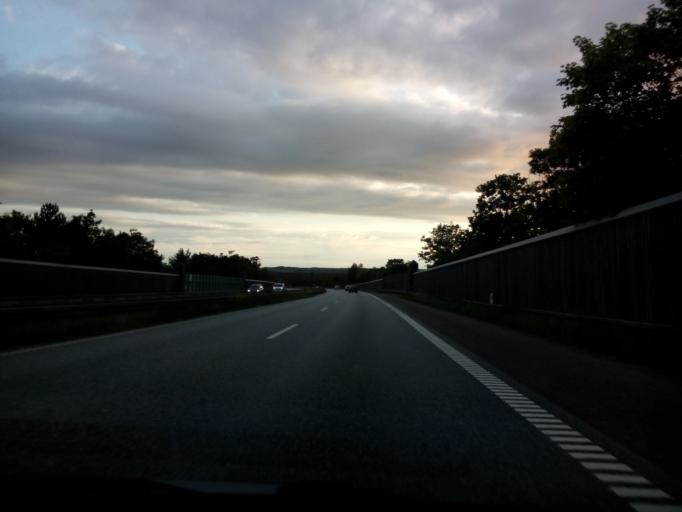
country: DK
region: North Denmark
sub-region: Alborg Kommune
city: Aalborg
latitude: 57.0122
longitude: 9.9275
